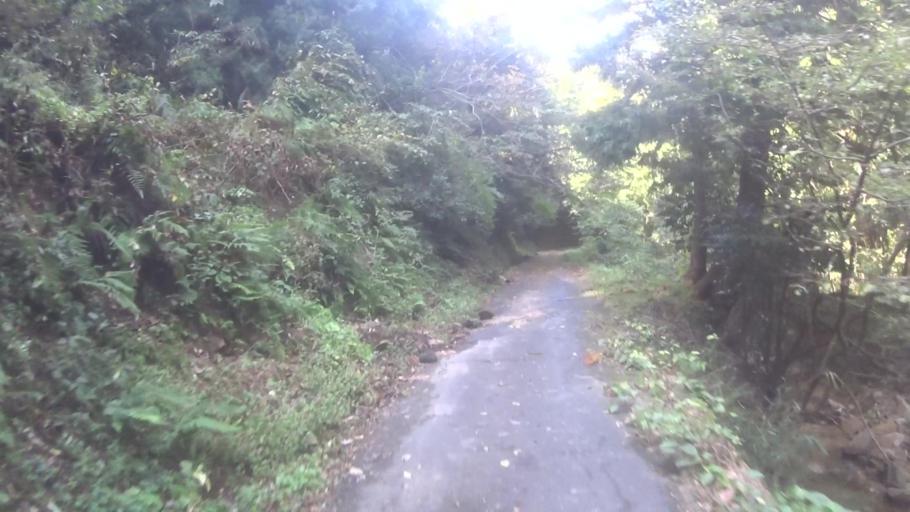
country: JP
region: Kyoto
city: Miyazu
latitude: 35.7012
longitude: 135.1228
